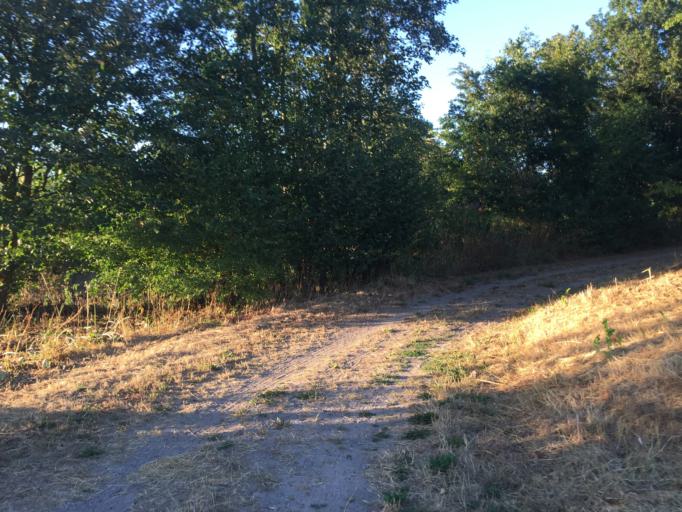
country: DK
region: South Denmark
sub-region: Odense Kommune
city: Bellinge
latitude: 55.3771
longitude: 10.3161
